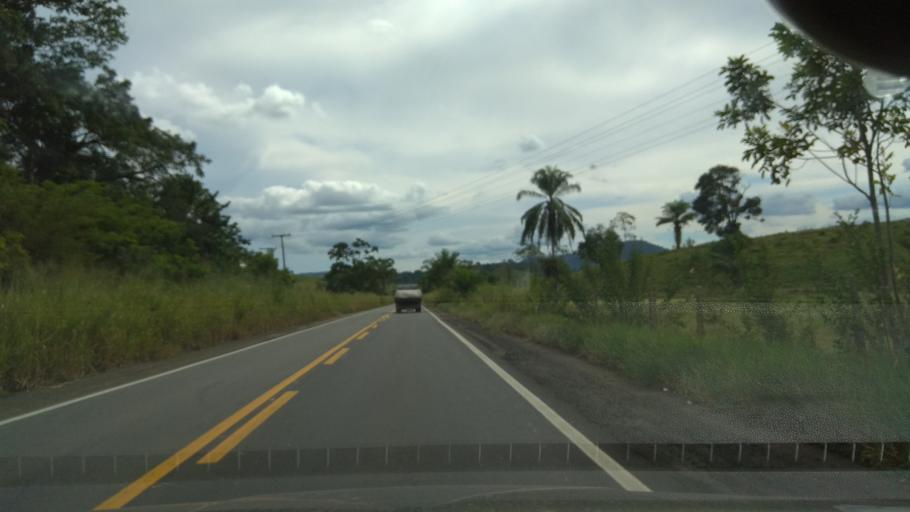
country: BR
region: Bahia
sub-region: Ipiau
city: Ipiau
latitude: -14.1941
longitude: -39.6465
